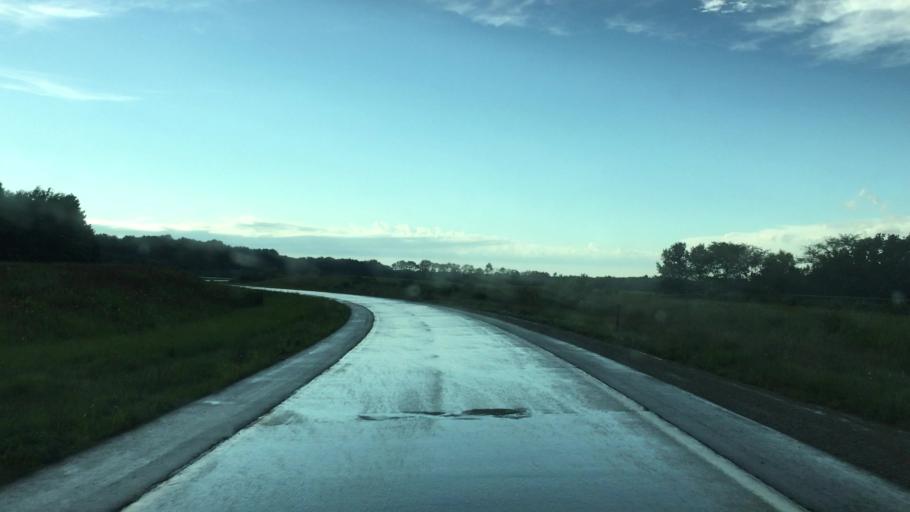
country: US
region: Iowa
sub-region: Henry County
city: Mount Pleasant
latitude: 40.9987
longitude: -91.5445
